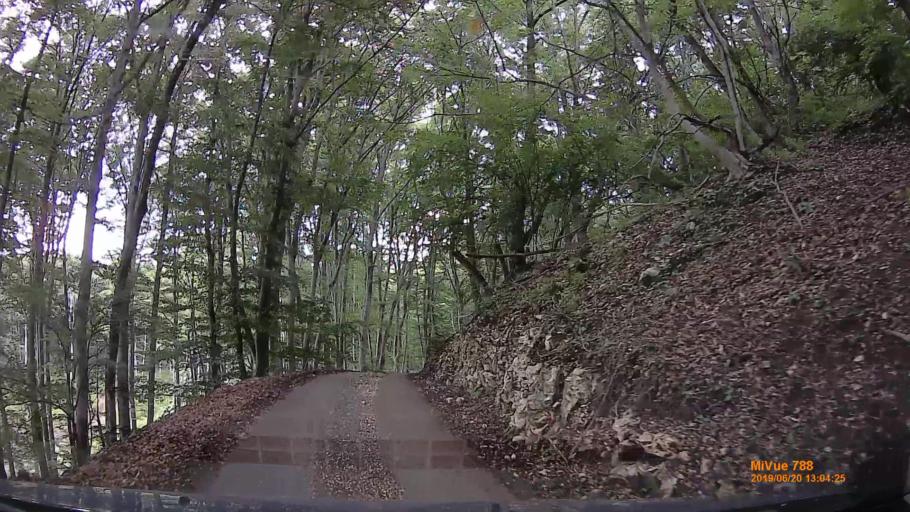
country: HU
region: Baranya
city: Hosszuheteny
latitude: 46.2137
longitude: 18.3614
